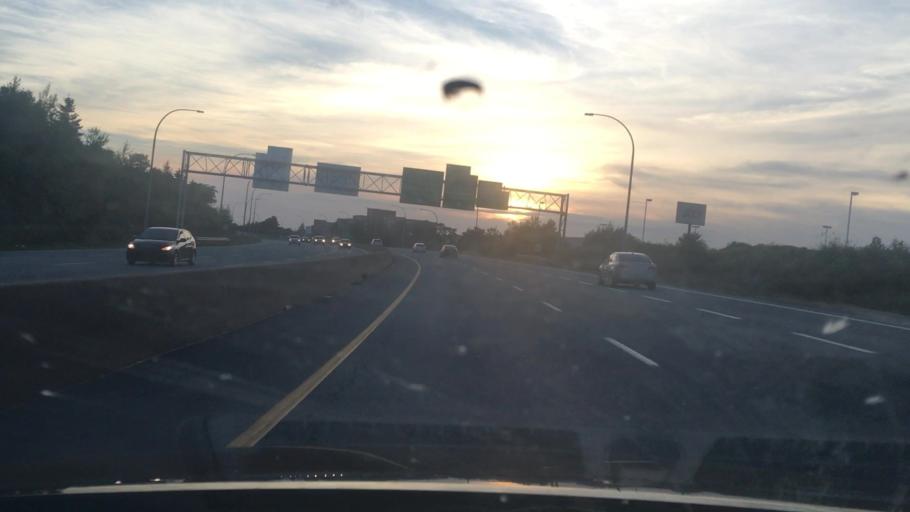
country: CA
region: Nova Scotia
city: Dartmouth
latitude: 44.6943
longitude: -63.5721
